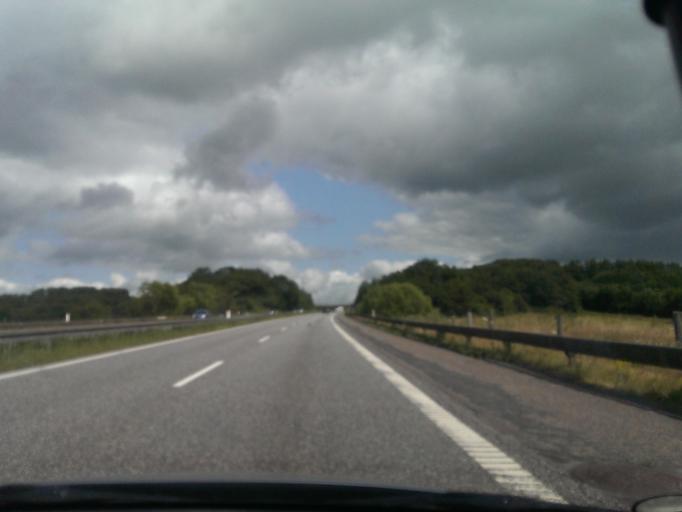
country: DK
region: North Denmark
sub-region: Mariagerfjord Kommune
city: Hobro
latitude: 56.6183
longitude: 9.7340
